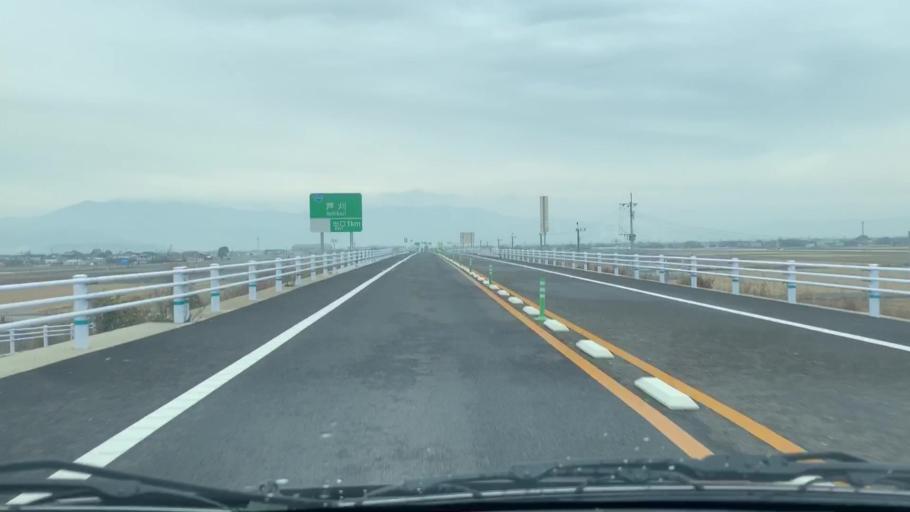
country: JP
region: Saga Prefecture
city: Saga-shi
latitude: 33.2091
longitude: 130.2150
